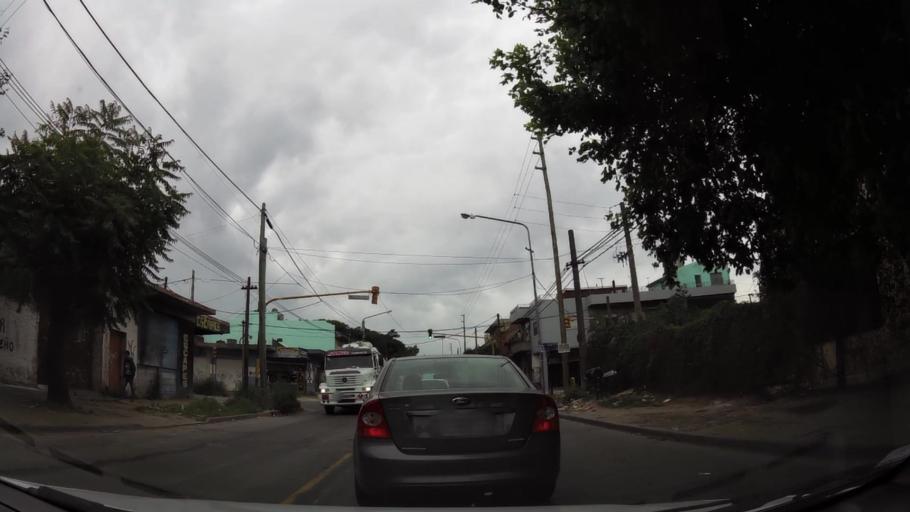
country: AR
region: Buenos Aires
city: San Justo
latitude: -34.6768
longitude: -58.5250
